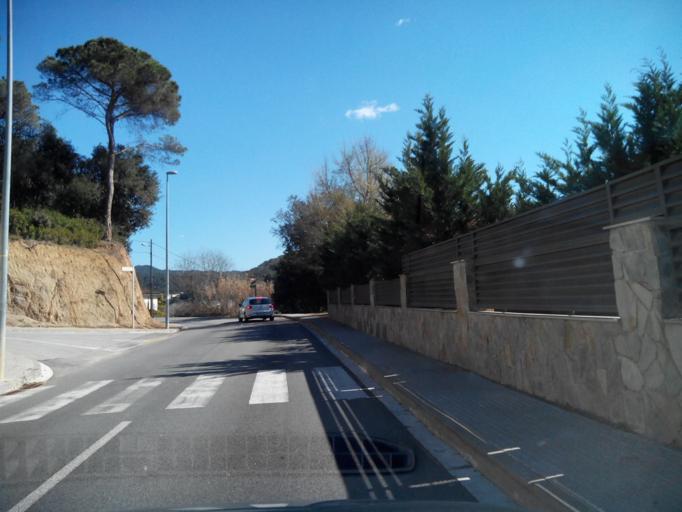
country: ES
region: Catalonia
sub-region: Provincia de Barcelona
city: Dosrius
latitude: 41.5961
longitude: 2.4056
